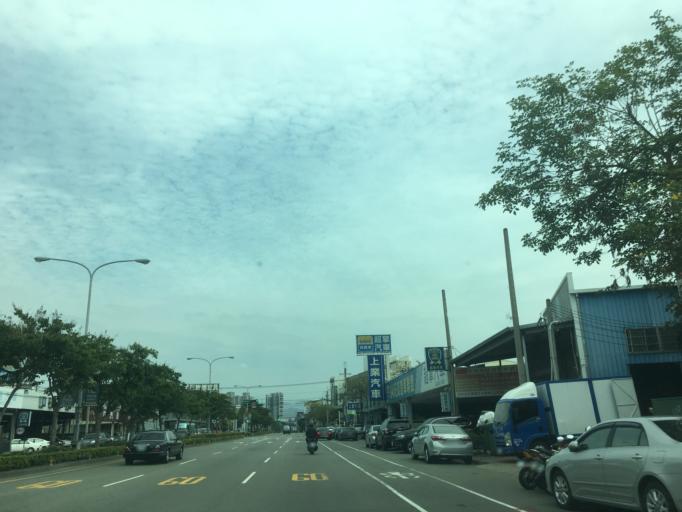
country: TW
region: Taiwan
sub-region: Taichung City
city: Taichung
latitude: 24.1059
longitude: 120.6661
